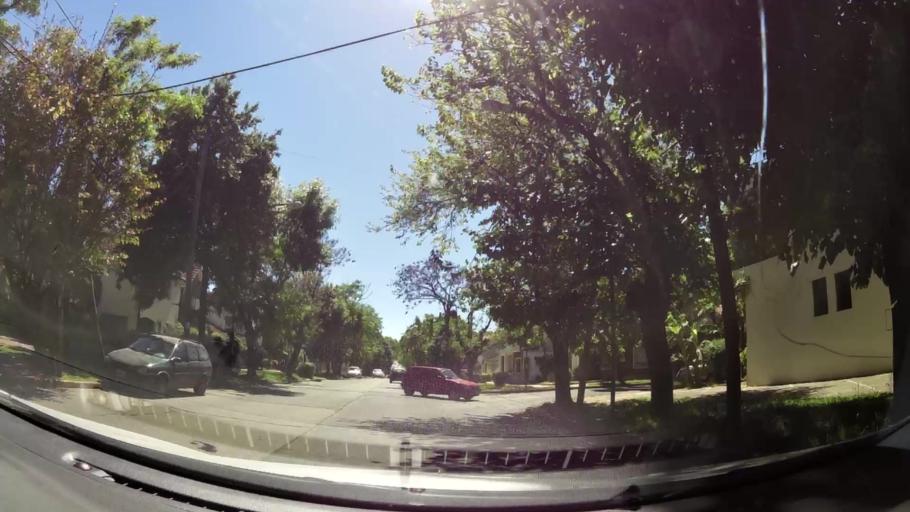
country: AR
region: Buenos Aires
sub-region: Partido de Vicente Lopez
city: Olivos
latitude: -34.4958
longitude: -58.4933
